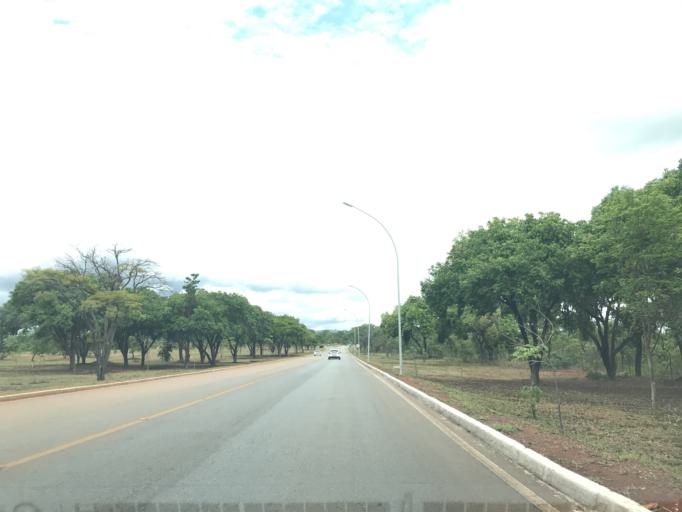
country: BR
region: Federal District
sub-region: Brasilia
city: Brasilia
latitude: -15.7960
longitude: -47.8393
